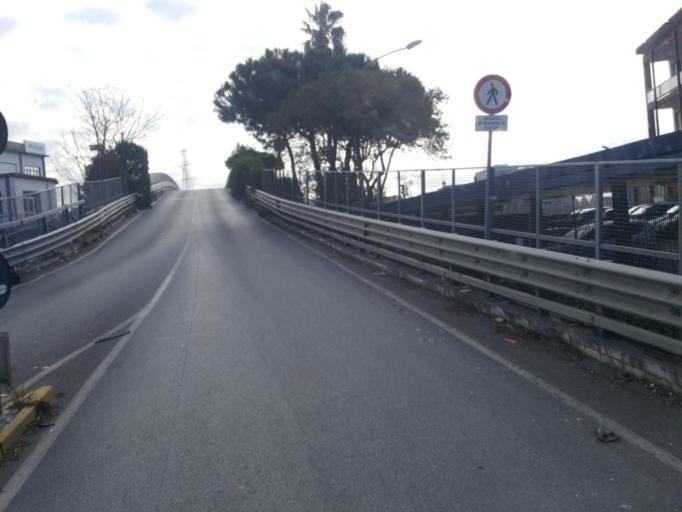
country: IT
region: Campania
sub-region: Provincia di Napoli
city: San Giorgio a Cremano
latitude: 40.8488
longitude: 14.3101
